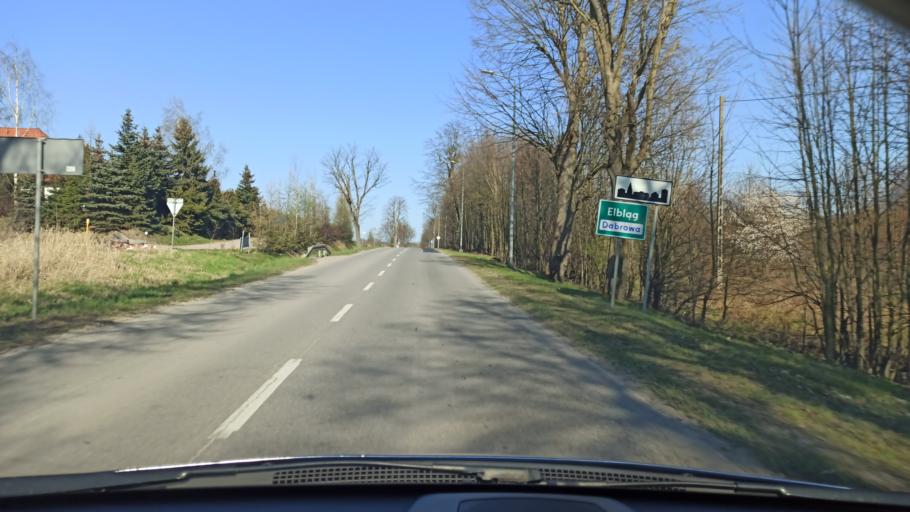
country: PL
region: Warmian-Masurian Voivodeship
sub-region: Powiat elblaski
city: Gronowo Gorne
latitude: 54.1861
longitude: 19.4655
